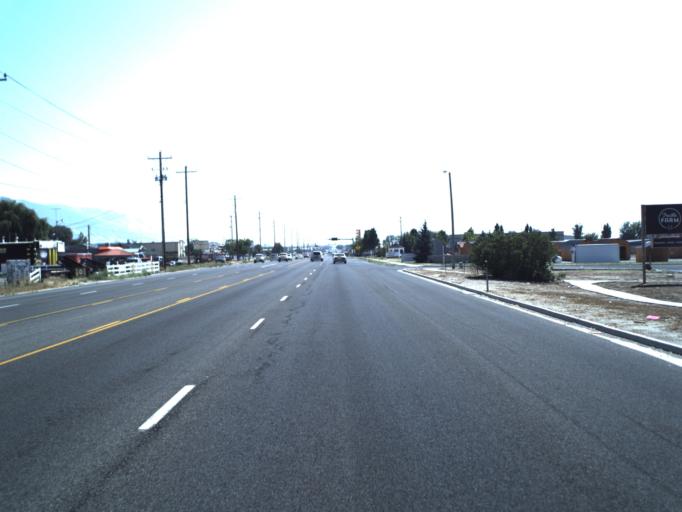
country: US
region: Utah
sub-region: Cache County
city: Hyde Park
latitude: 41.8042
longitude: -111.8335
